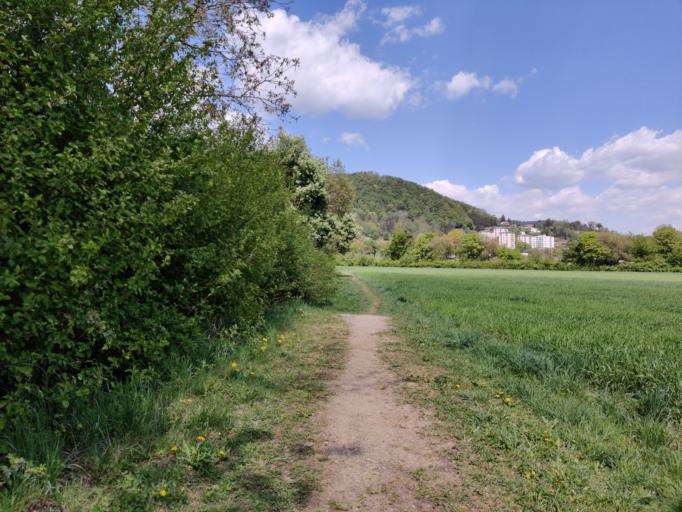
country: AT
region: Styria
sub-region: Graz Stadt
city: Wetzelsdorf
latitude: 47.0406
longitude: 15.3879
